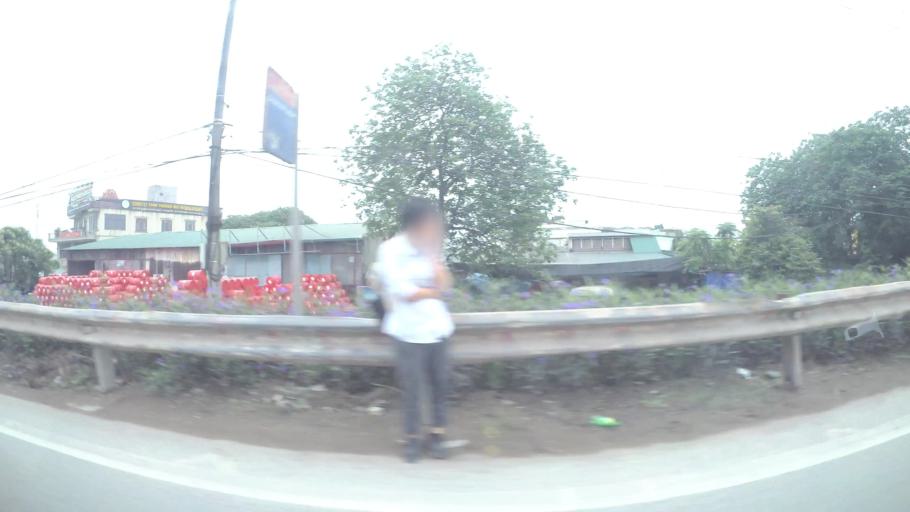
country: VN
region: Ha Noi
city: Hai BaTrung
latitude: 20.9893
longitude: 105.8939
